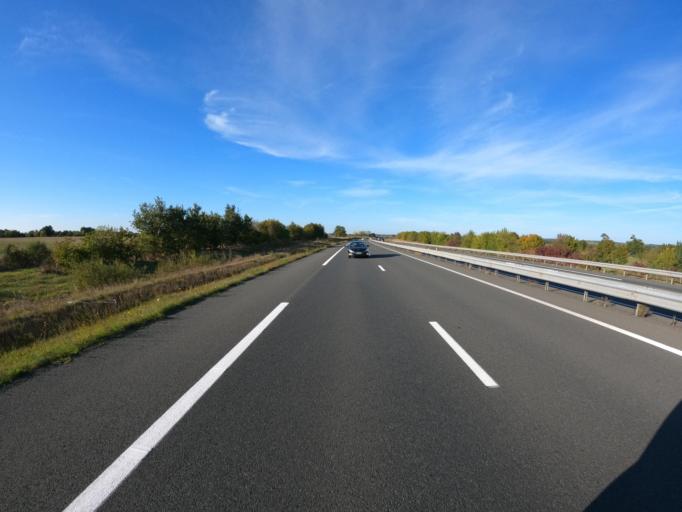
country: FR
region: Pays de la Loire
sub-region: Departement de Maine-et-Loire
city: Saint-Lambert-du-Lattay
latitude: 47.2796
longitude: -0.6164
